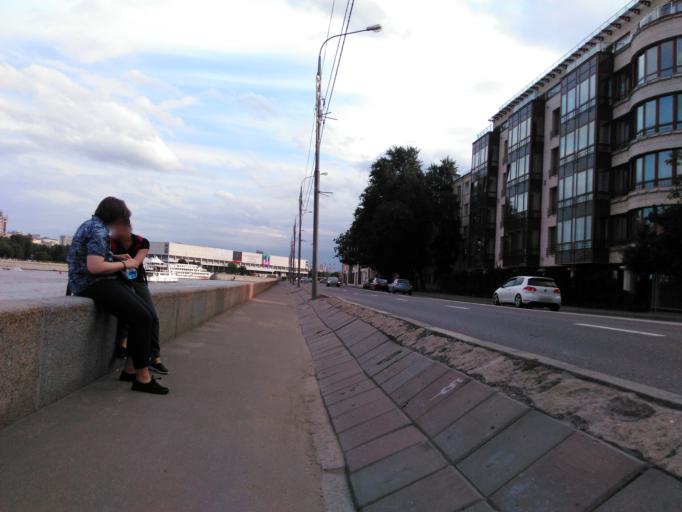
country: RU
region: Moscow
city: Moscow
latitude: 55.7413
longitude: 37.6068
